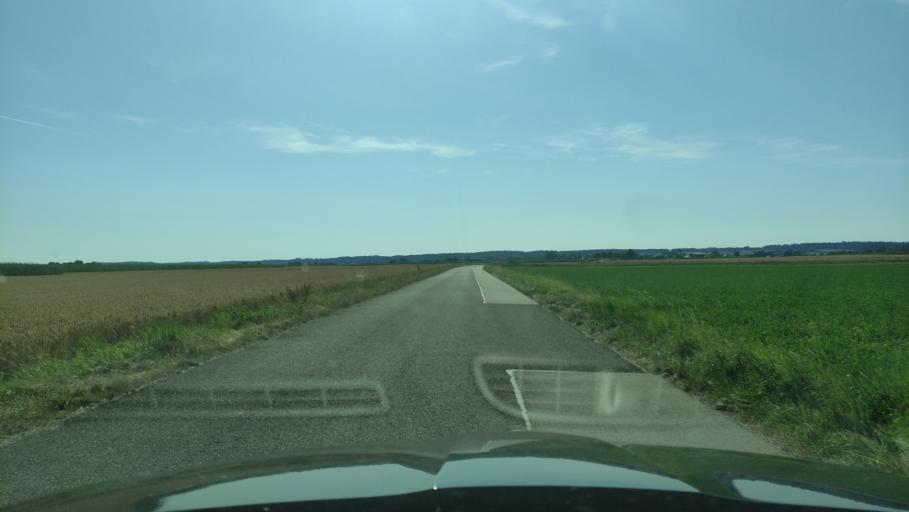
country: DE
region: Bavaria
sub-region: Swabia
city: Ebershausen
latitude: 48.2076
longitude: 10.3054
